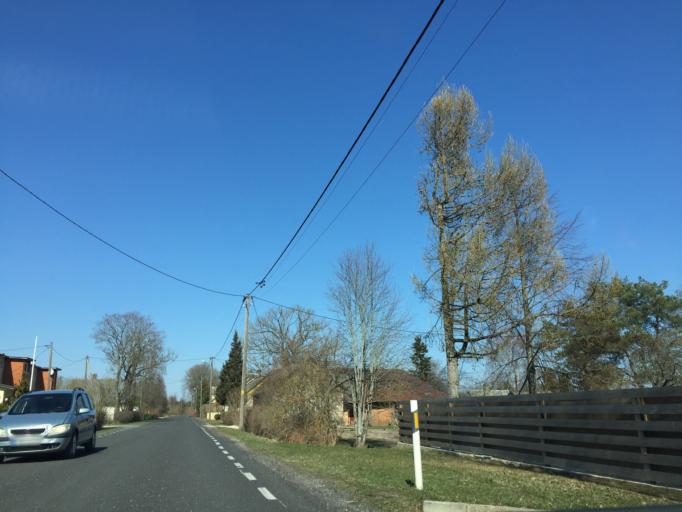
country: EE
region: Jogevamaa
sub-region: Mustvee linn
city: Mustvee
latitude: 58.8590
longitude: 26.9511
